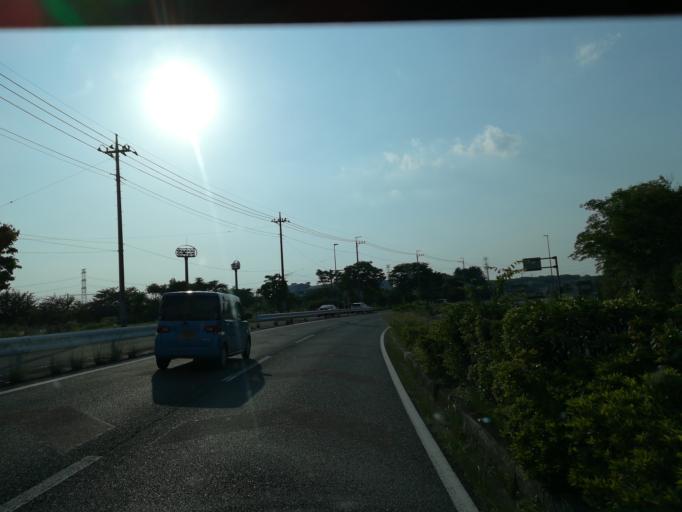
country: JP
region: Saitama
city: Kumagaya
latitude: 36.0672
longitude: 139.3637
